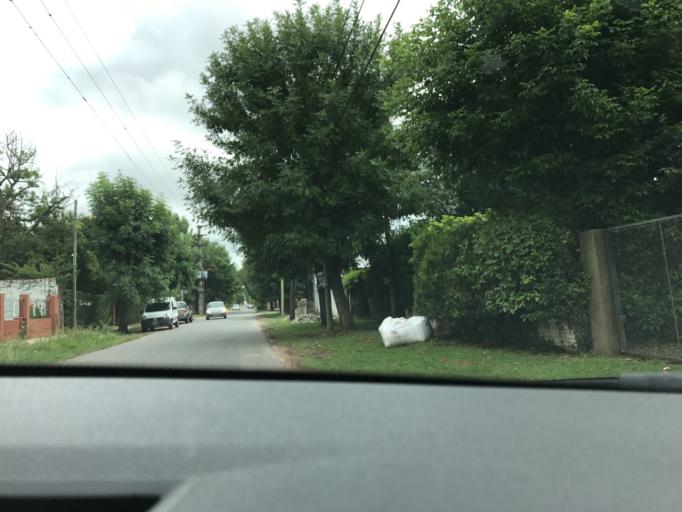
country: AR
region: Buenos Aires
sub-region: Partido de La Plata
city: La Plata
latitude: -34.8517
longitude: -58.0805
